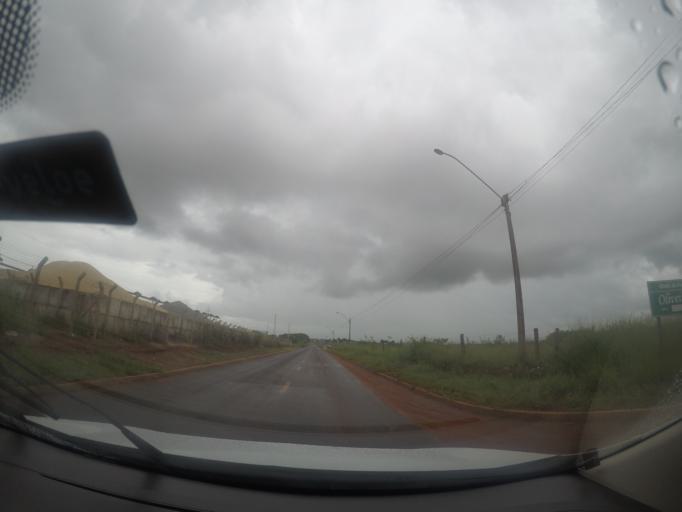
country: BR
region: Goias
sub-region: Trindade
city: Trindade
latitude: -16.6411
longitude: -49.4056
